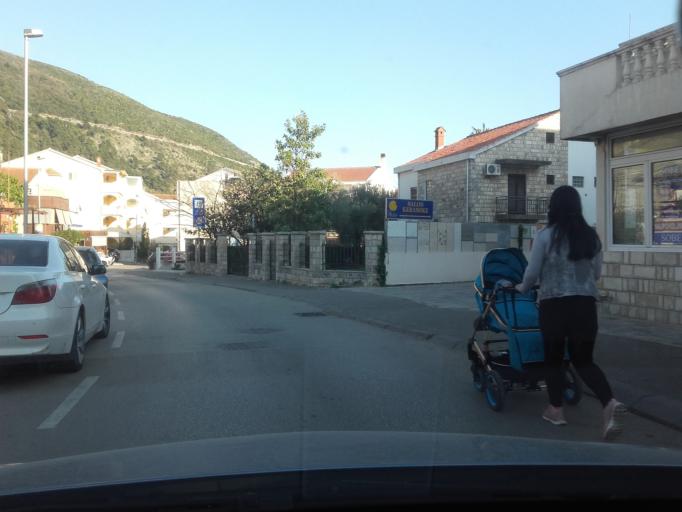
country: ME
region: Budva
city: Budva
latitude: 42.2922
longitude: 18.8457
